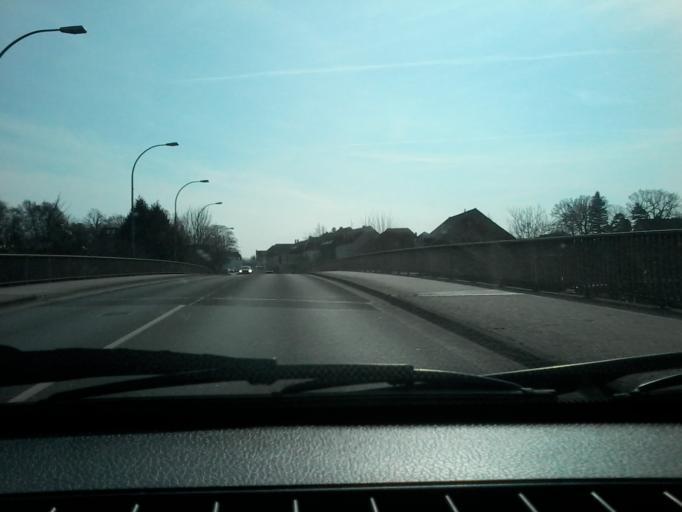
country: DE
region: Lower Saxony
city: Achim
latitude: 53.0163
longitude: 9.0317
